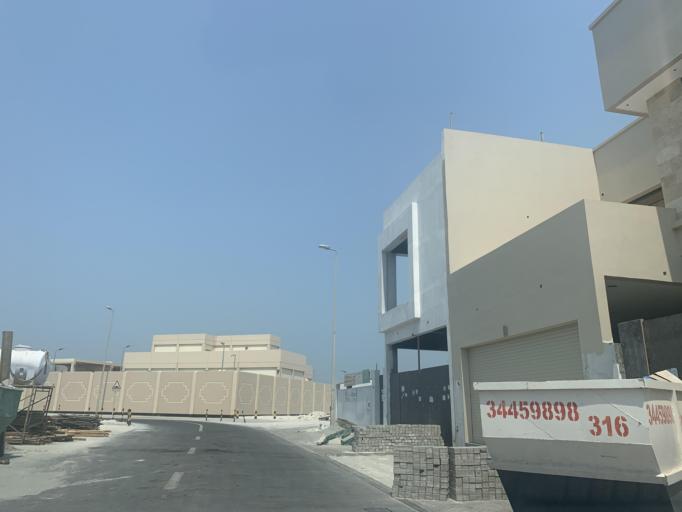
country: BH
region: Muharraq
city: Al Hadd
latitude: 26.2349
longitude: 50.6618
